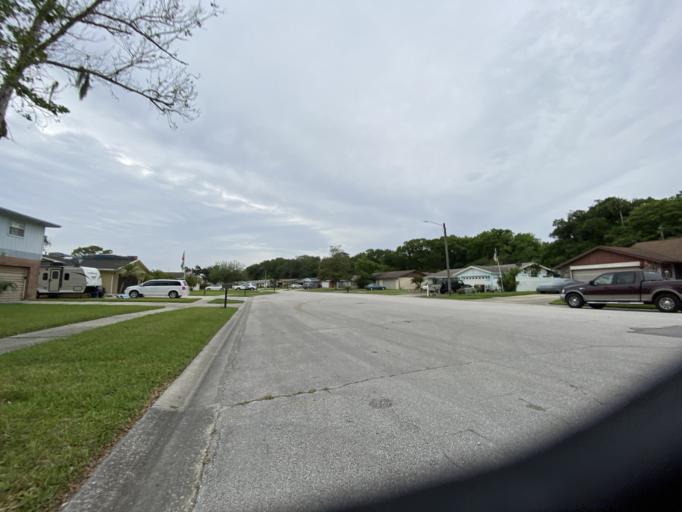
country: US
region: Florida
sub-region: Volusia County
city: South Daytona
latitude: 29.1580
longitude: -81.0067
